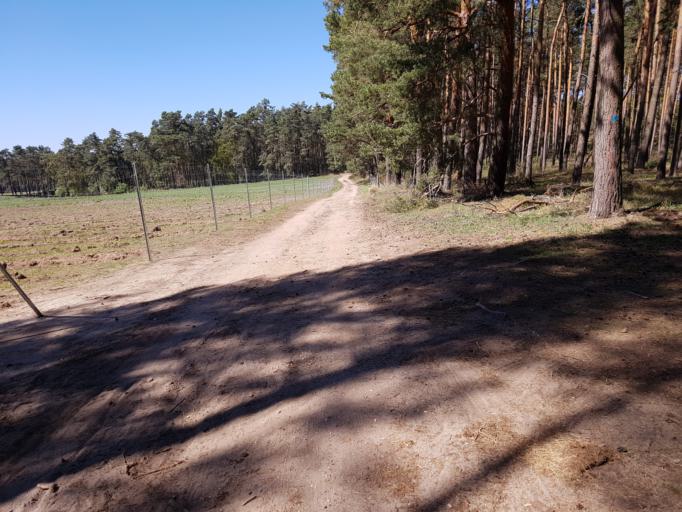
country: DE
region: Brandenburg
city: Groden
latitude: 51.3926
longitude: 13.5678
